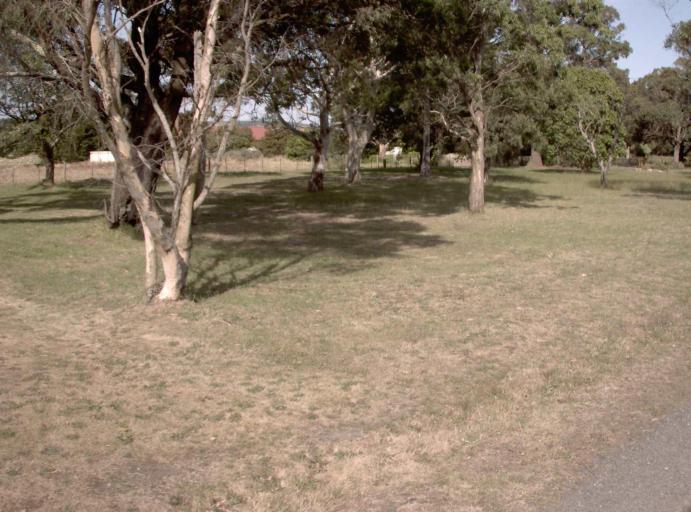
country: AU
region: Victoria
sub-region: Latrobe
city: Moe
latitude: -38.1647
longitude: 146.2748
